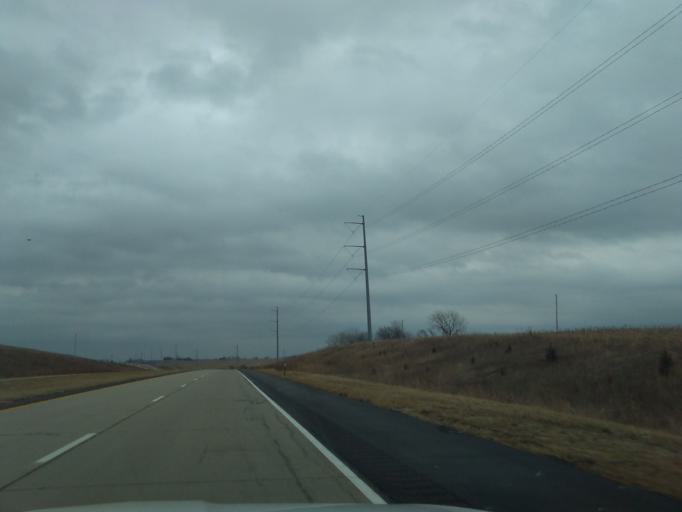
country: US
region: Nebraska
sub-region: Otoe County
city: Syracuse
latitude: 40.6691
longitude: -96.1593
